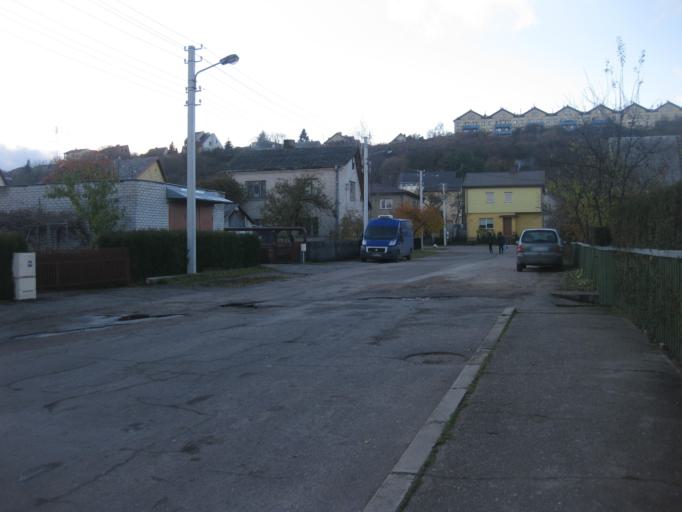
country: LT
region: Kauno apskritis
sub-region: Kaunas
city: Silainiai
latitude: 54.9246
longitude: 23.9027
